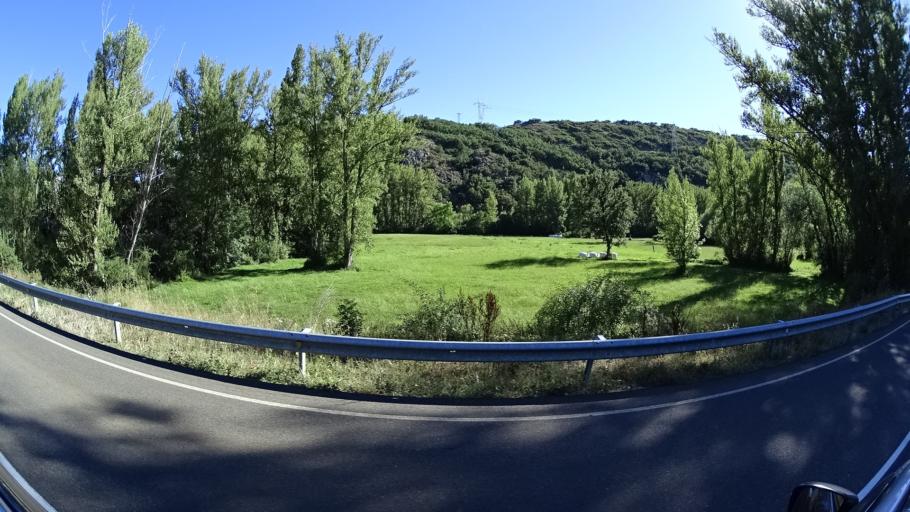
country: ES
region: Castille and Leon
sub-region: Provincia de Leon
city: La Pola de Gordon
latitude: 42.8626
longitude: -5.6768
